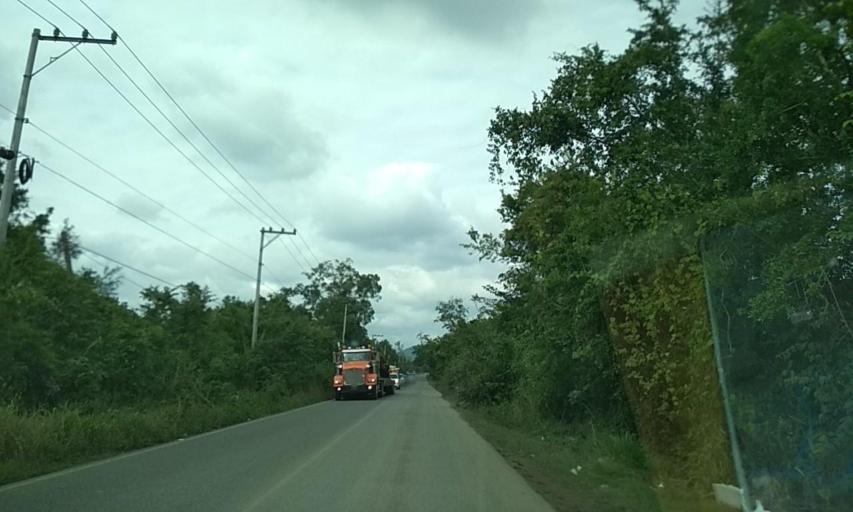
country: MX
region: Veracruz
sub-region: Papantla
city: El Chote
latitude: 20.3780
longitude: -97.3355
